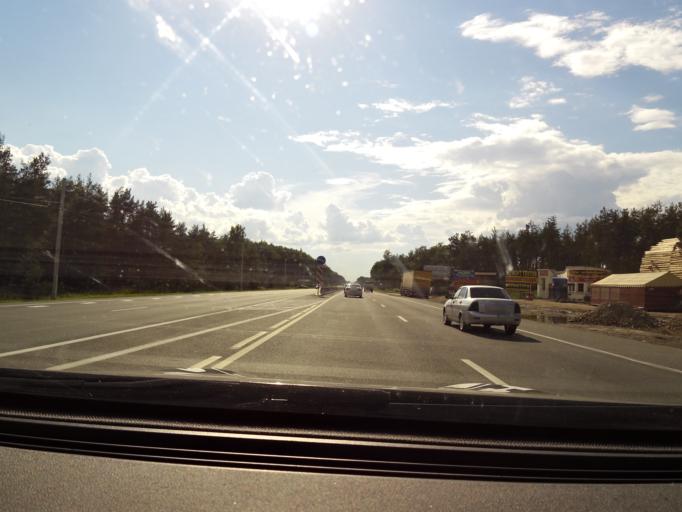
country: RU
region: Nizjnij Novgorod
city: Gorbatovka
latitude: 56.3086
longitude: 43.7382
